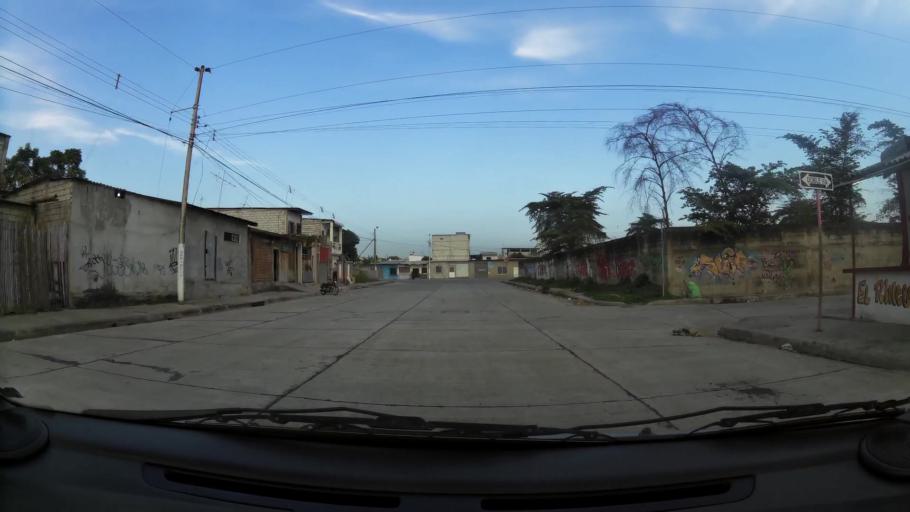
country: EC
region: Guayas
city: Eloy Alfaro
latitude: -2.0897
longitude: -79.8993
